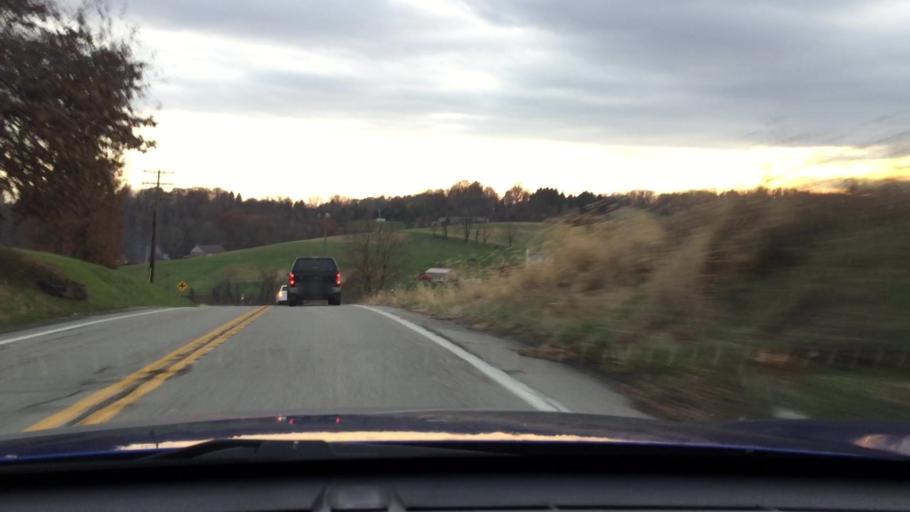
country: US
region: Pennsylvania
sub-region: Allegheny County
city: Elizabeth
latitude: 40.2435
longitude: -79.8605
